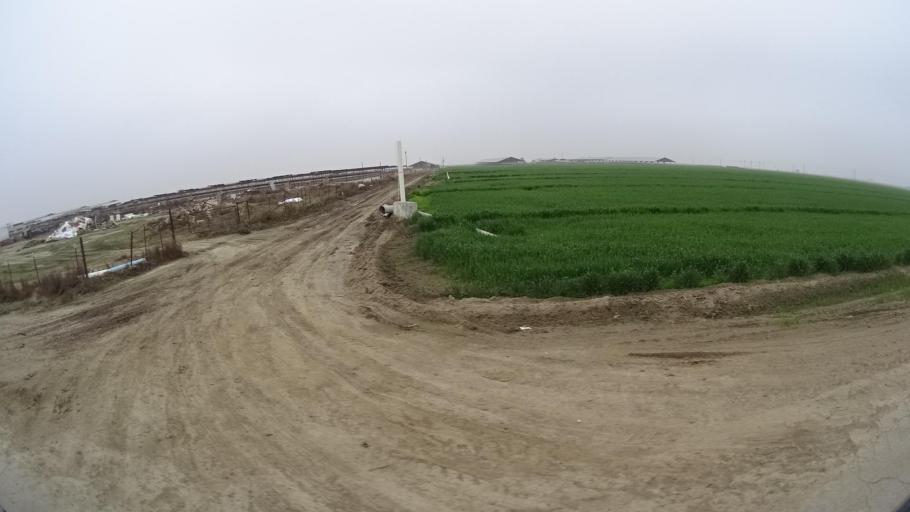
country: US
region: California
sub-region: Kern County
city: Wasco
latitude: 35.7140
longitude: -119.4194
